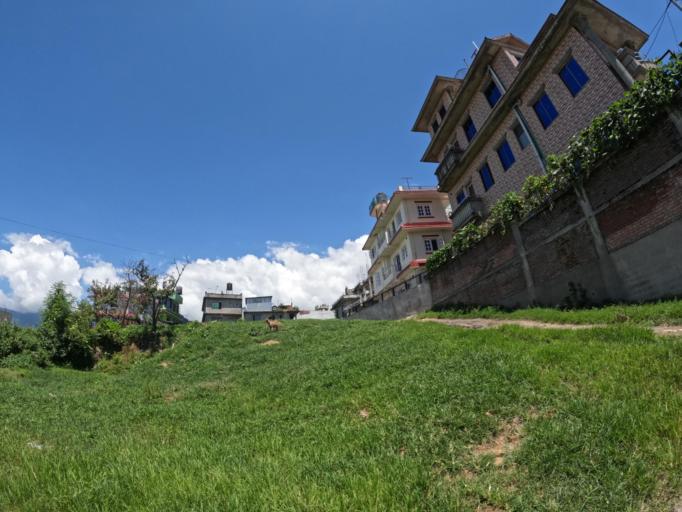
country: NP
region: Central Region
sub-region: Bagmati Zone
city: Kathmandu
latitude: 27.7441
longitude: 85.3251
